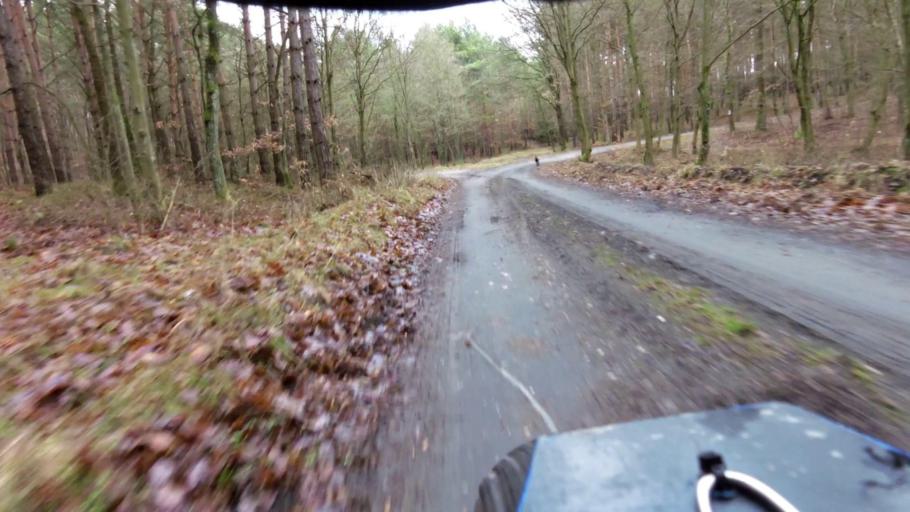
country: PL
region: Lubusz
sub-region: Powiat gorzowski
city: Bogdaniec
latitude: 52.6943
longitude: 15.0287
